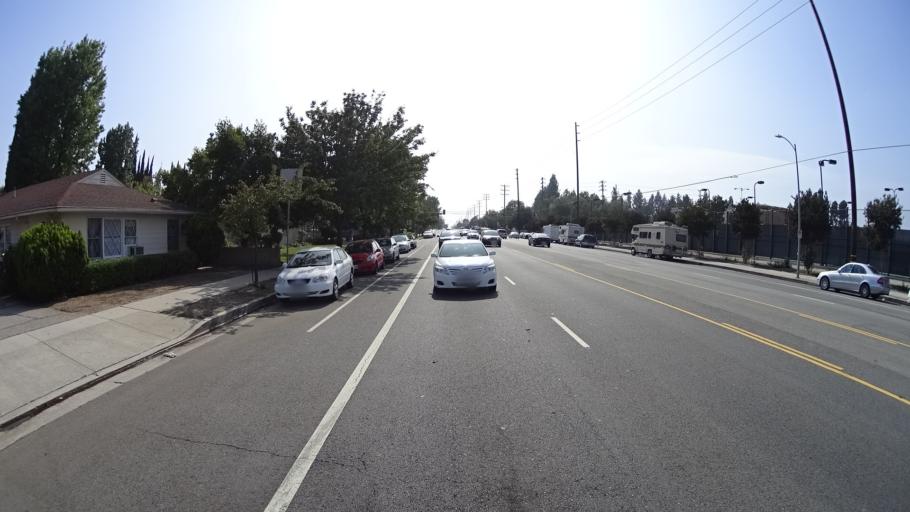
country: US
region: California
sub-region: Los Angeles County
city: Van Nuys
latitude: 34.1721
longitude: -118.4170
